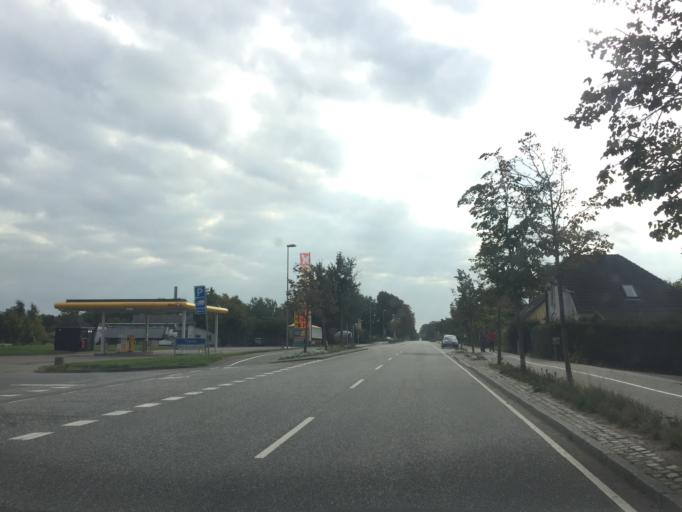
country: DK
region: Zealand
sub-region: Vordingborg Kommune
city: Praesto
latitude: 55.1646
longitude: 11.9802
